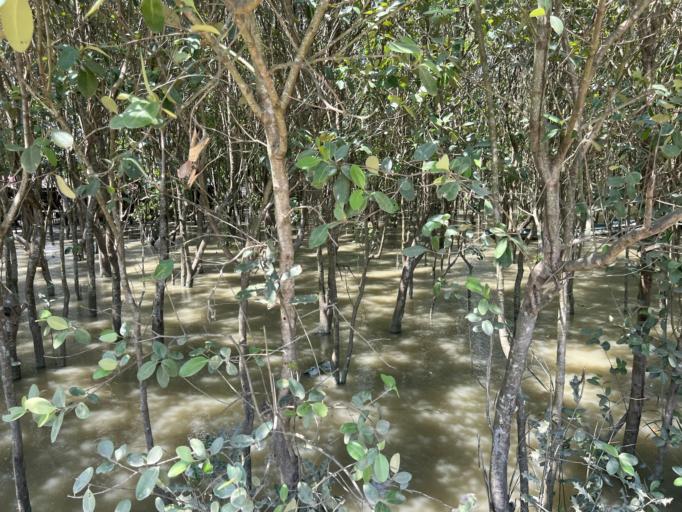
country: MM
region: Ayeyarwady
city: Pyapon
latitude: 15.9900
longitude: 95.5964
